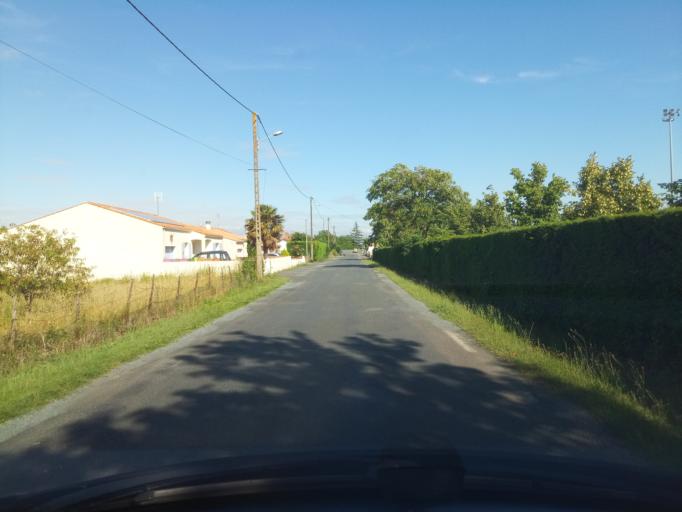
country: FR
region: Poitou-Charentes
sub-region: Departement de la Charente-Maritime
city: Marans
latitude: 46.3035
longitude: -0.9927
